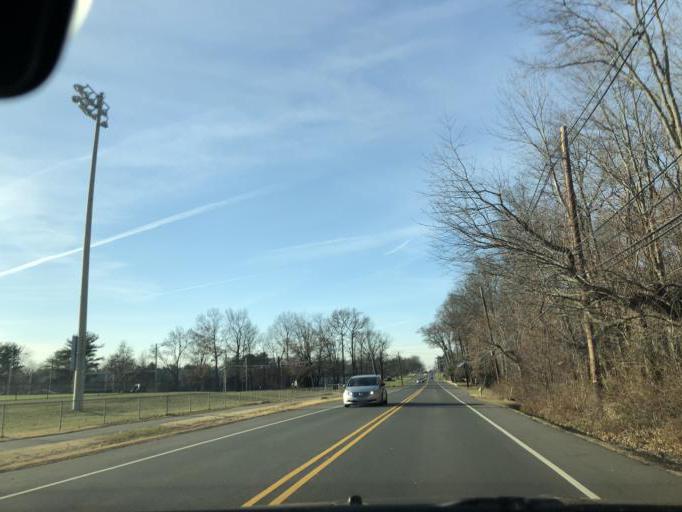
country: US
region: New Jersey
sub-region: Burlington County
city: Moorestown-Lenola
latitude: 39.9764
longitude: -74.9838
